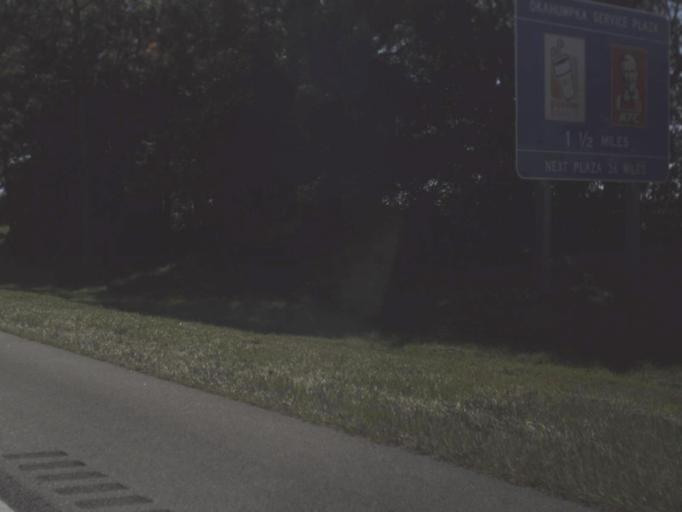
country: US
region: Florida
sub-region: Sumter County
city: Wildwood
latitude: 28.8032
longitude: -82.0030
